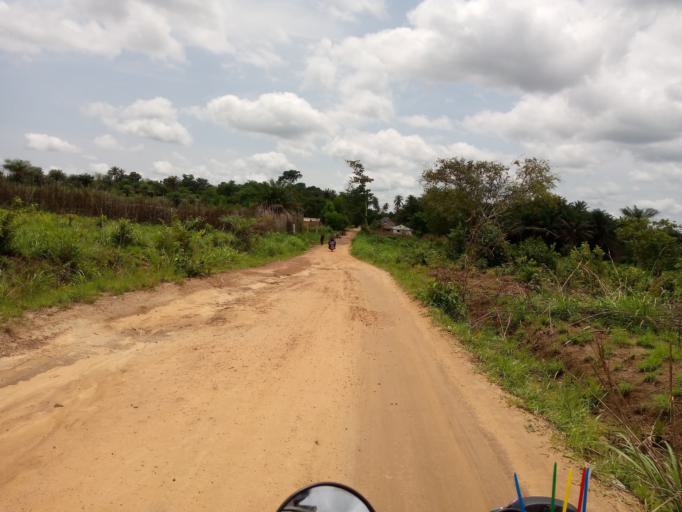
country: SL
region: Western Area
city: Waterloo
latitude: 8.3313
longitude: -12.9410
